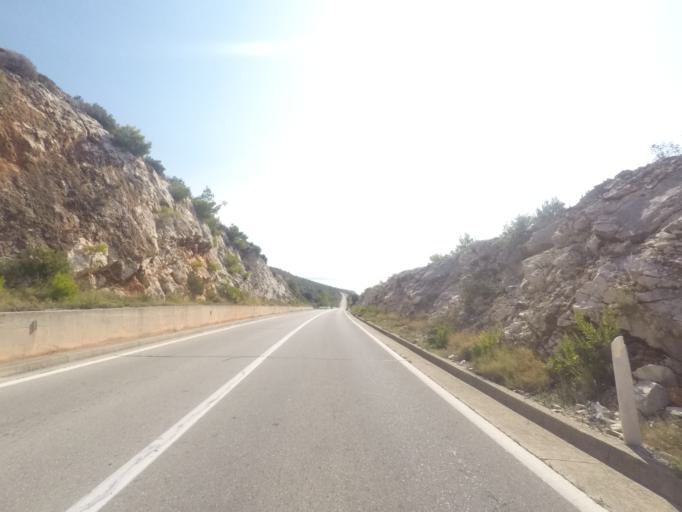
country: HR
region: Splitsko-Dalmatinska
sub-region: Grad Hvar
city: Hvar
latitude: 43.1514
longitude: 16.5171
